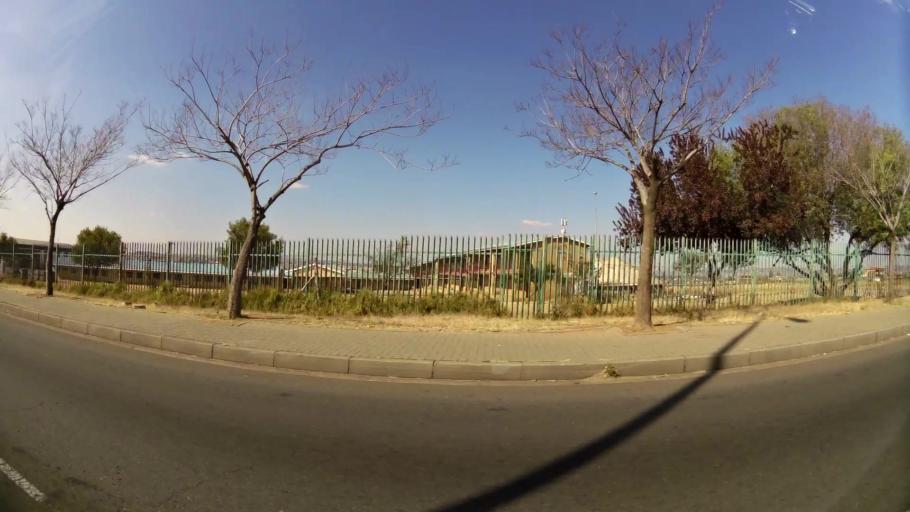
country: ZA
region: Gauteng
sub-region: City of Johannesburg Metropolitan Municipality
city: Soweto
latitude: -26.2722
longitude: 27.8737
